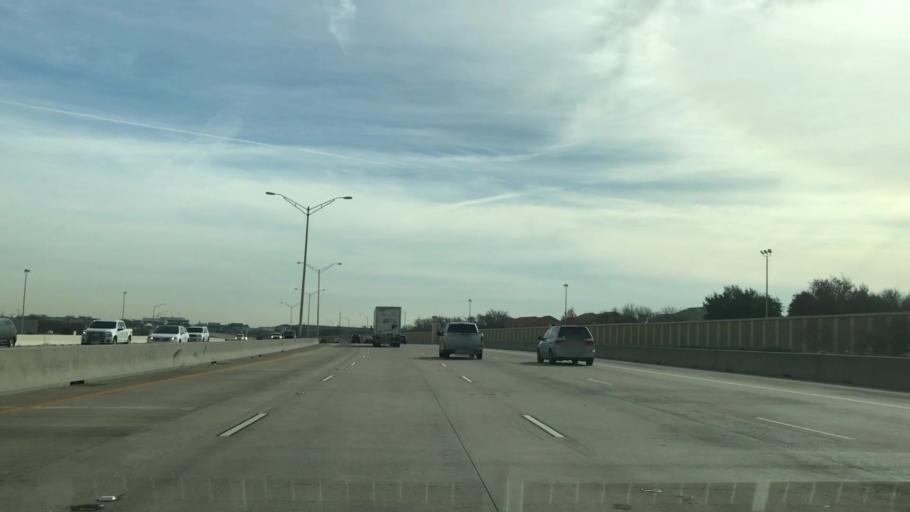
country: US
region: Texas
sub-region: Dallas County
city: Addison
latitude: 33.0017
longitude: -96.7753
